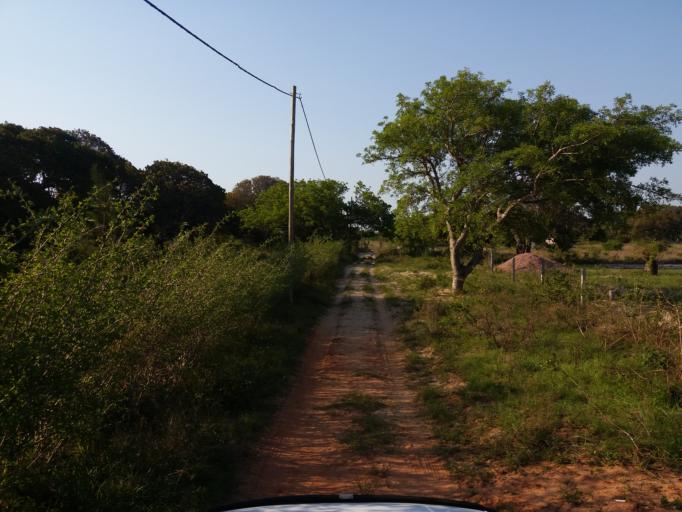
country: MZ
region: Maputo City
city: Maputo
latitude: -25.7600
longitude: 32.6076
